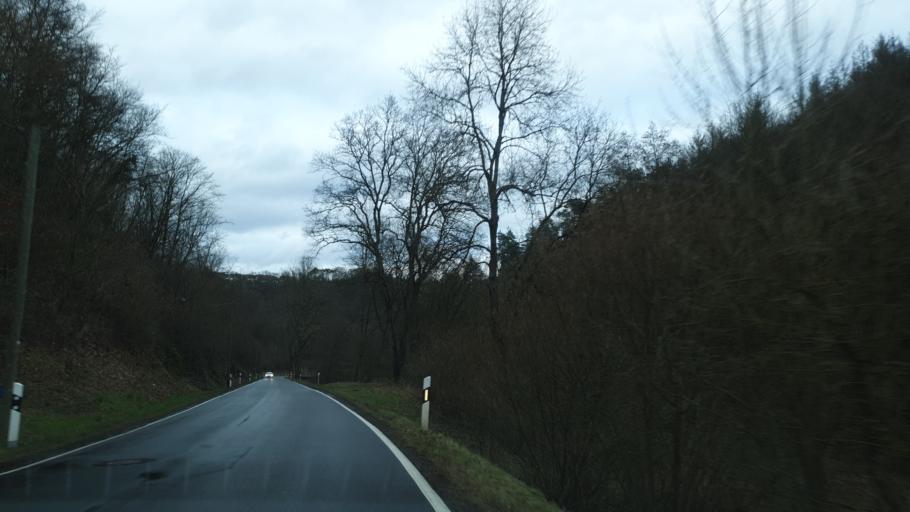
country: DE
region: Rheinland-Pfalz
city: Biebrich
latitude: 50.3145
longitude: 7.9389
